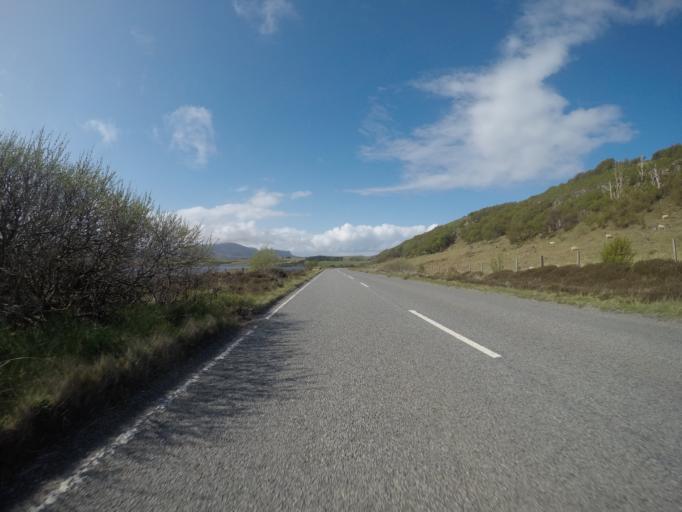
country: GB
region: Scotland
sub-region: Highland
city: Portree
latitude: 57.6038
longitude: -6.1689
